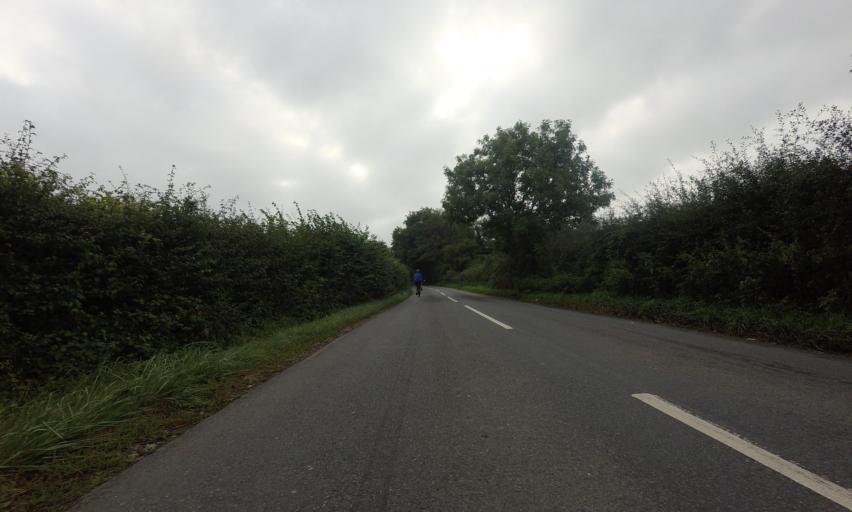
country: GB
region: England
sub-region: Gloucestershire
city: Gotherington
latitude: 51.9681
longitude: -2.0270
